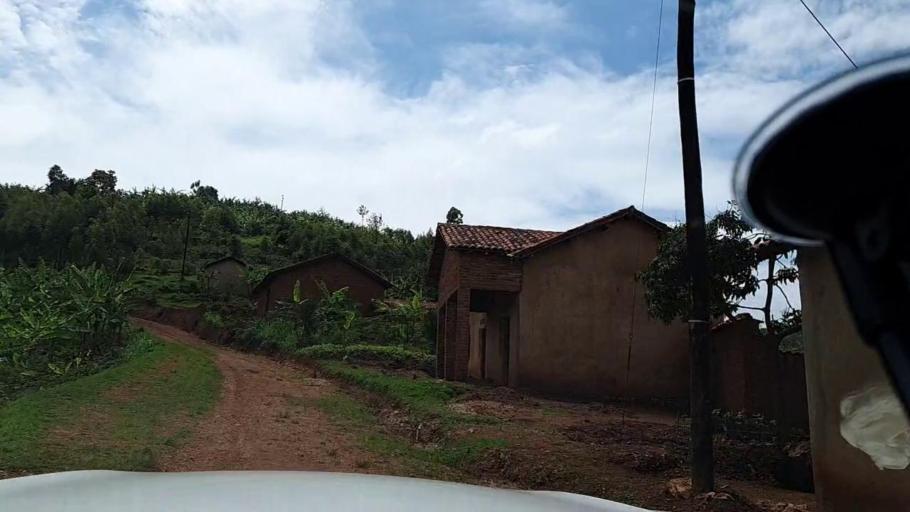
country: RW
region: Southern Province
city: Gitarama
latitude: -2.0753
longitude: 29.6692
